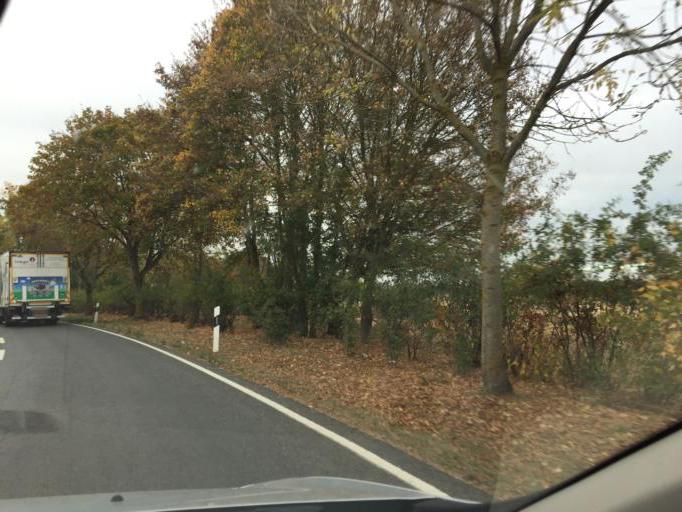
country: LU
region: Luxembourg
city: Capellen
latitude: 49.6495
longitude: 5.9890
